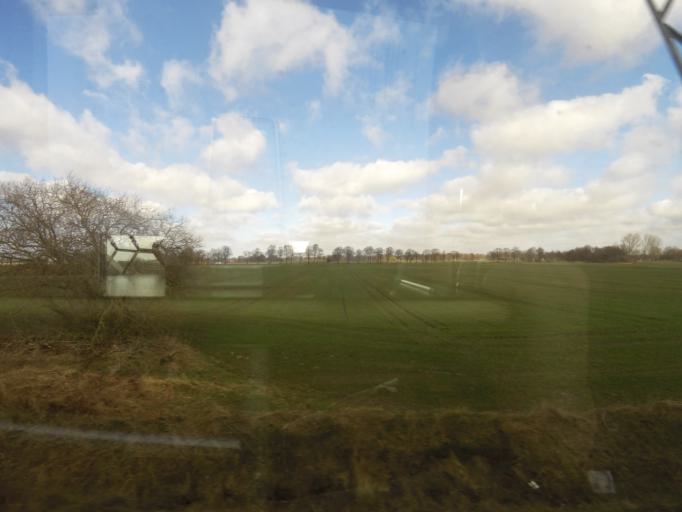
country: DE
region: Lower Saxony
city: Oyten
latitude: 53.0890
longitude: 9.0568
